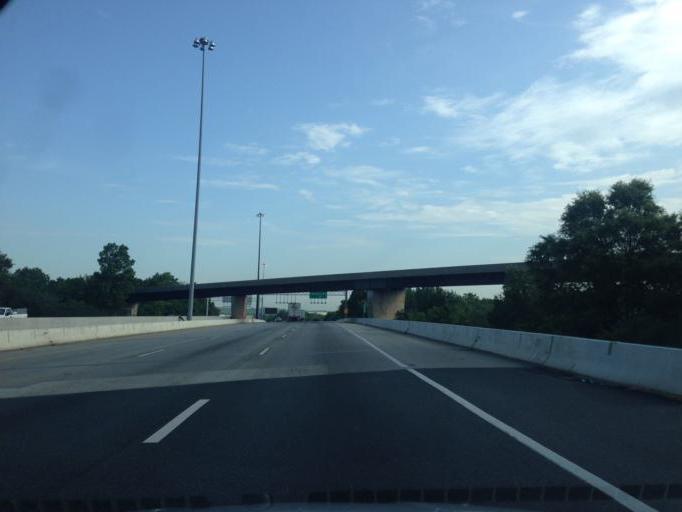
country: US
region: Maryland
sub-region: Baltimore County
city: Rosedale
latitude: 39.3043
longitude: -76.5304
